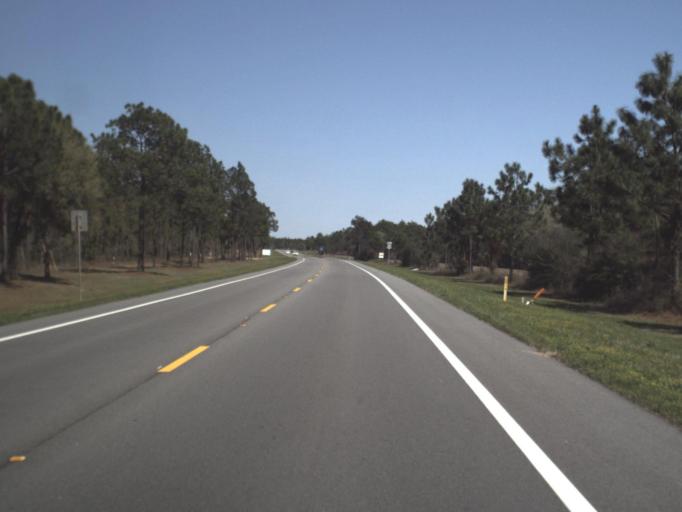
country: US
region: Florida
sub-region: Okaloosa County
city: Crestview
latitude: 30.7426
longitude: -86.3894
